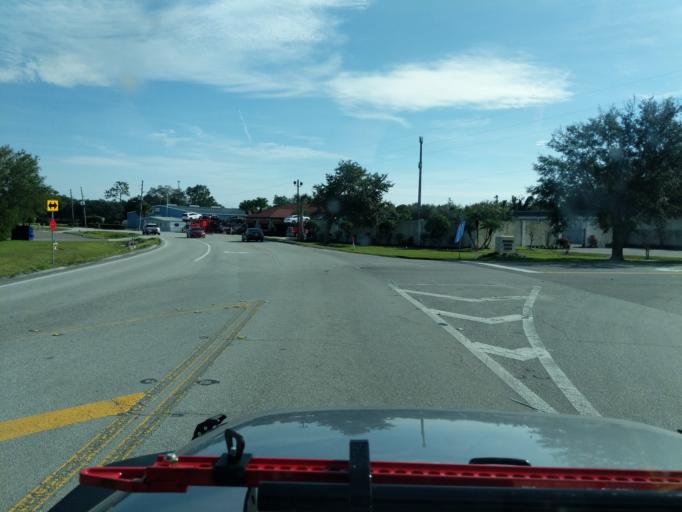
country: US
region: Florida
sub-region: Orange County
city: Ocoee
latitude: 28.5570
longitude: -81.5462
